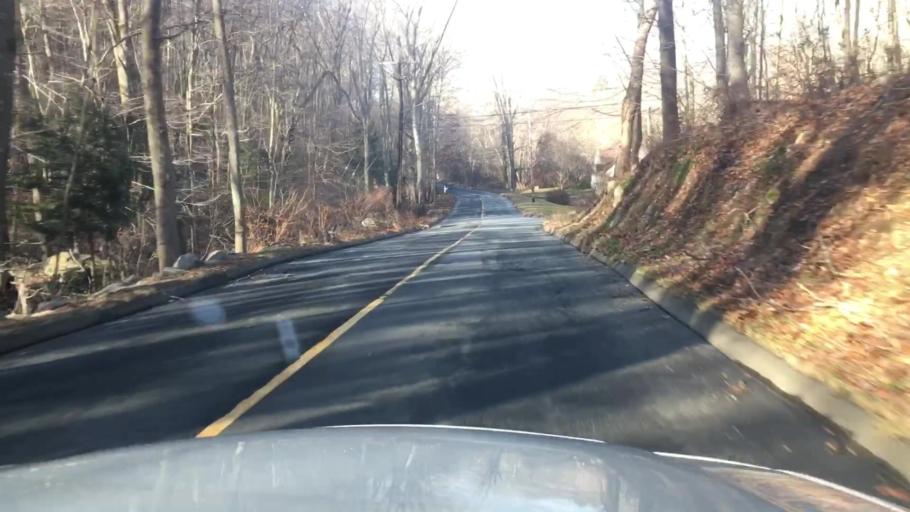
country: US
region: Connecticut
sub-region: Middlesex County
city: Deep River Center
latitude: 41.3792
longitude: -72.4130
